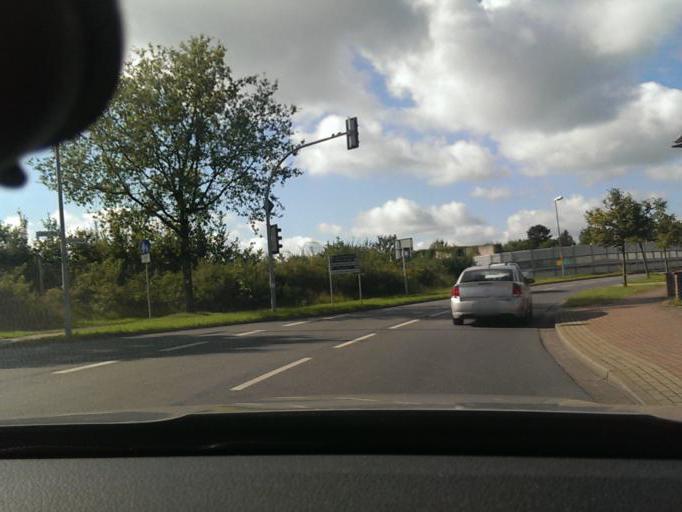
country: DE
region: Lower Saxony
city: Isernhagen Farster Bauerschaft
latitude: 52.4738
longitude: 9.8557
